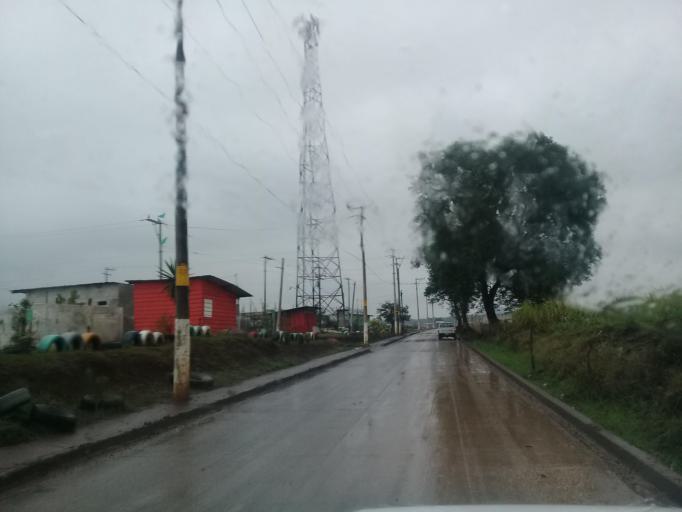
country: MX
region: Veracruz
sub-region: Cordoba
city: San Jose de Tapia
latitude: 18.8523
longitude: -96.9573
